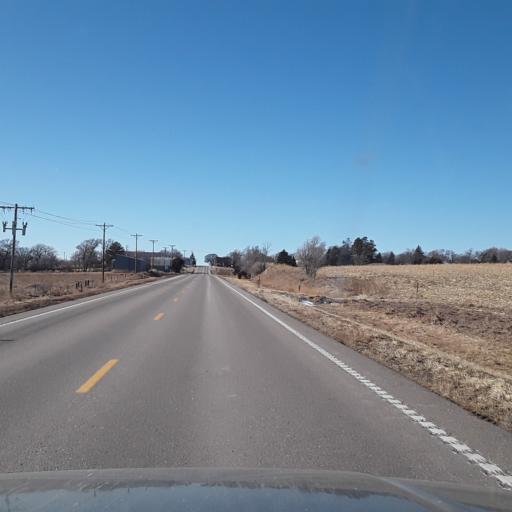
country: US
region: Nebraska
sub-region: Dawson County
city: Gothenburg
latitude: 40.7057
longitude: -100.2073
